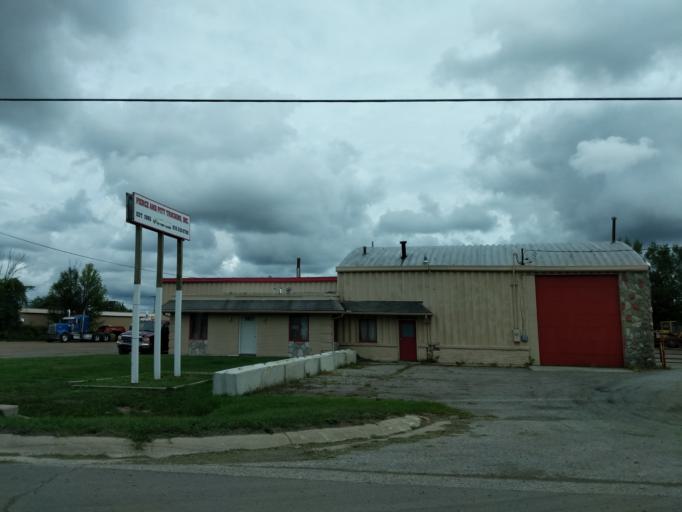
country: US
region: Michigan
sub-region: Lapeer County
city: Almont
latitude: 42.9305
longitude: -83.0524
